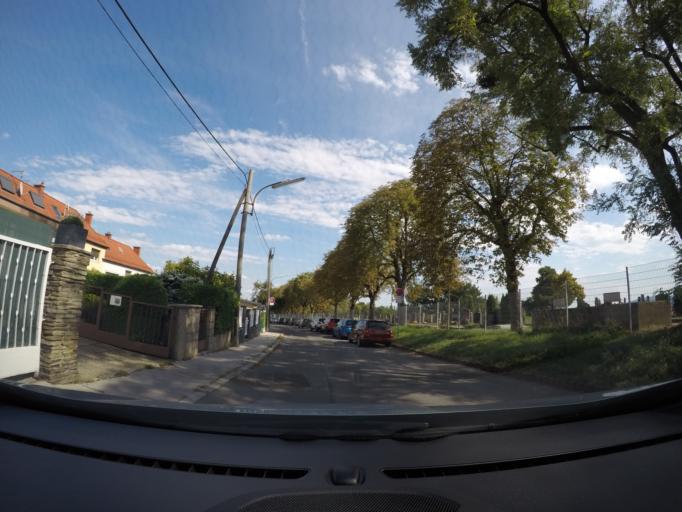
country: AT
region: Lower Austria
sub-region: Politischer Bezirk Modling
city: Perchtoldsdorf
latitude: 48.2039
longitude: 16.2839
